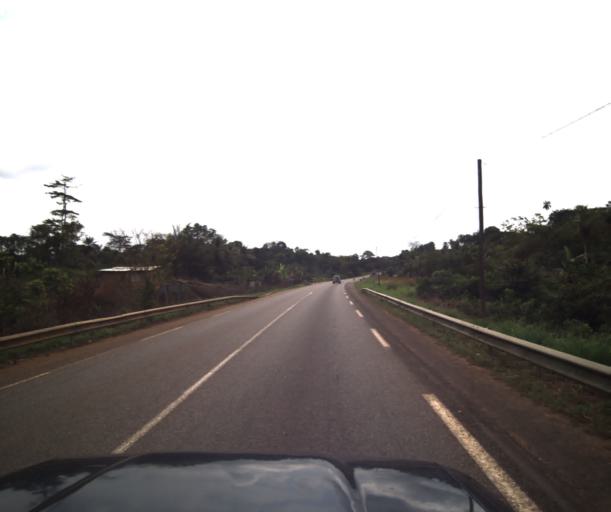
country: CM
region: Littoral
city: Edea
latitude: 3.8386
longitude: 10.4507
